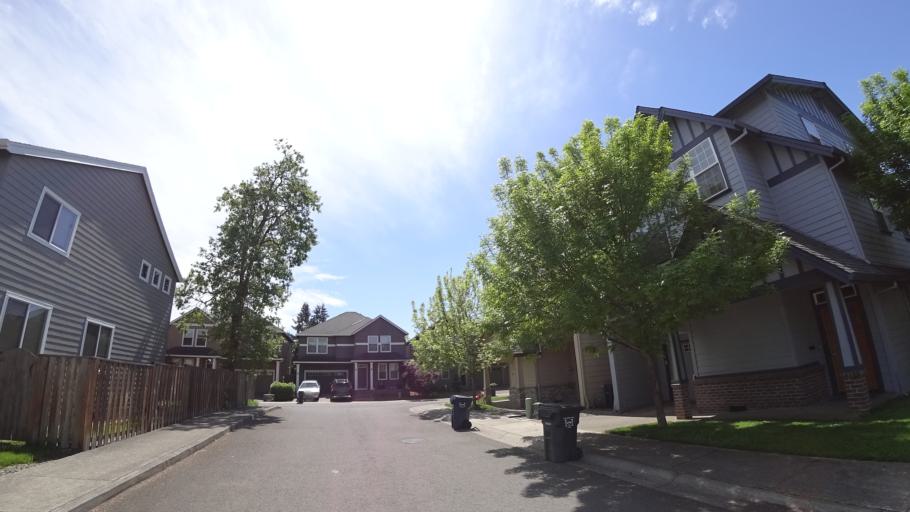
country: US
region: Oregon
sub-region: Washington County
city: Aloha
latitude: 45.4883
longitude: -122.8501
